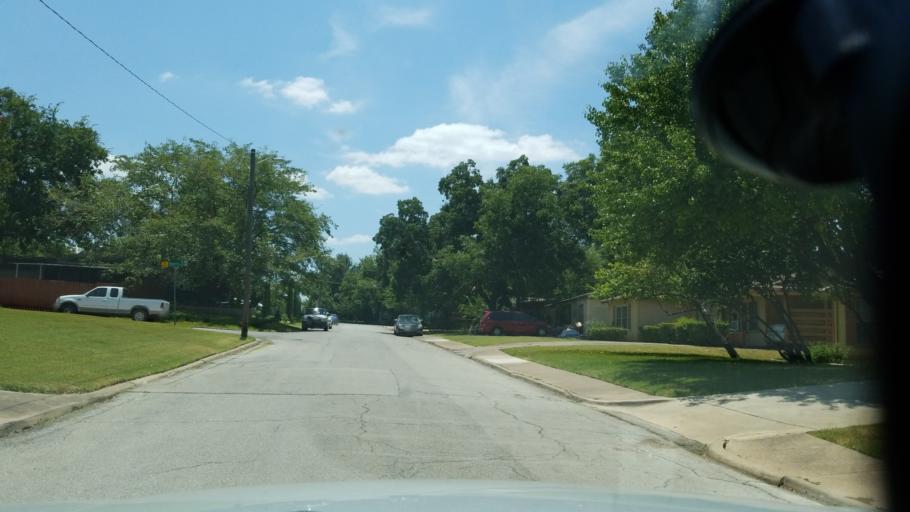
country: US
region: Texas
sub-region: Dallas County
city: Grand Prairie
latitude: 32.7567
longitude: -96.9727
